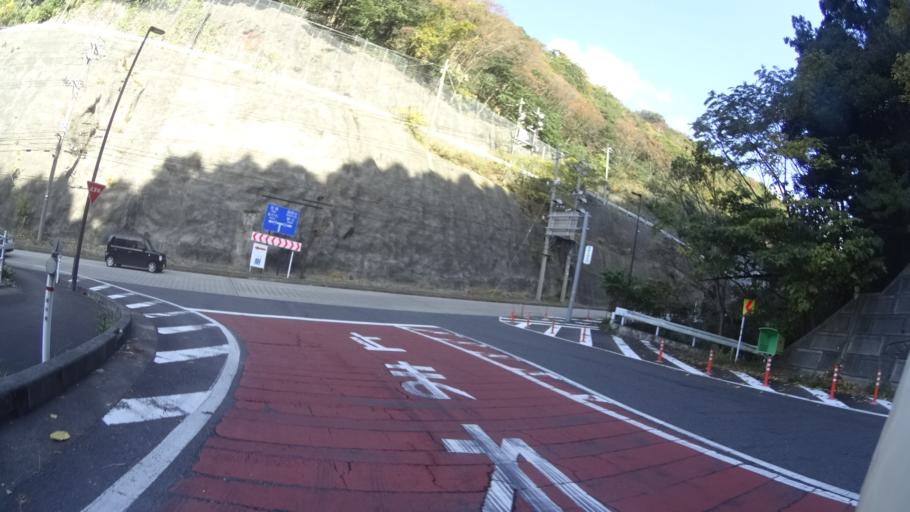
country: JP
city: Asahi
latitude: 35.9366
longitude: 136.0006
